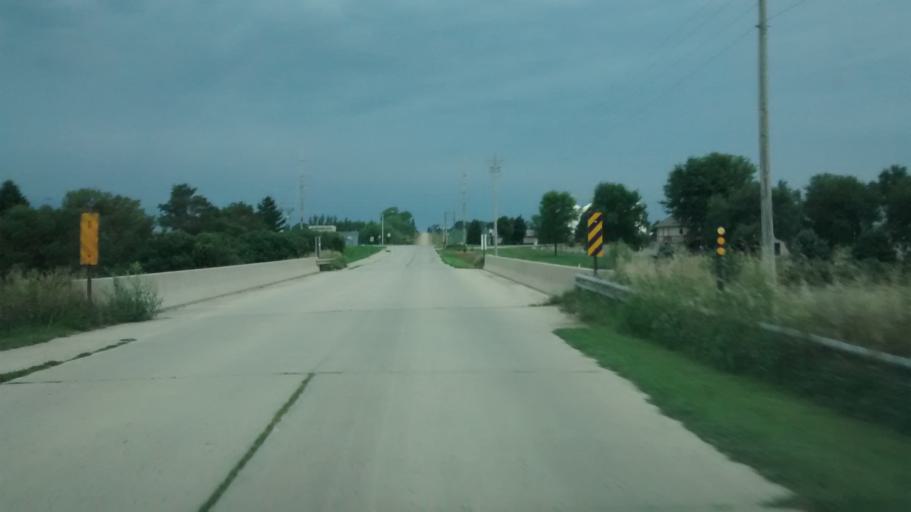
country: US
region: Iowa
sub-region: Plymouth County
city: Kingsley
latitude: 42.5848
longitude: -95.9780
